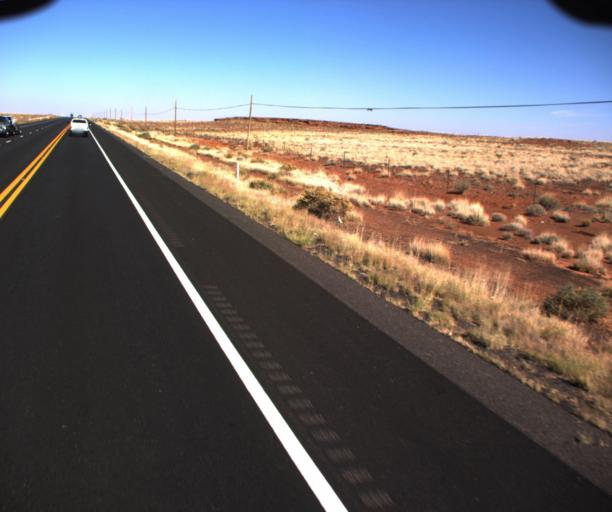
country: US
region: Arizona
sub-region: Coconino County
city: Tuba City
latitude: 35.7090
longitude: -111.4931
